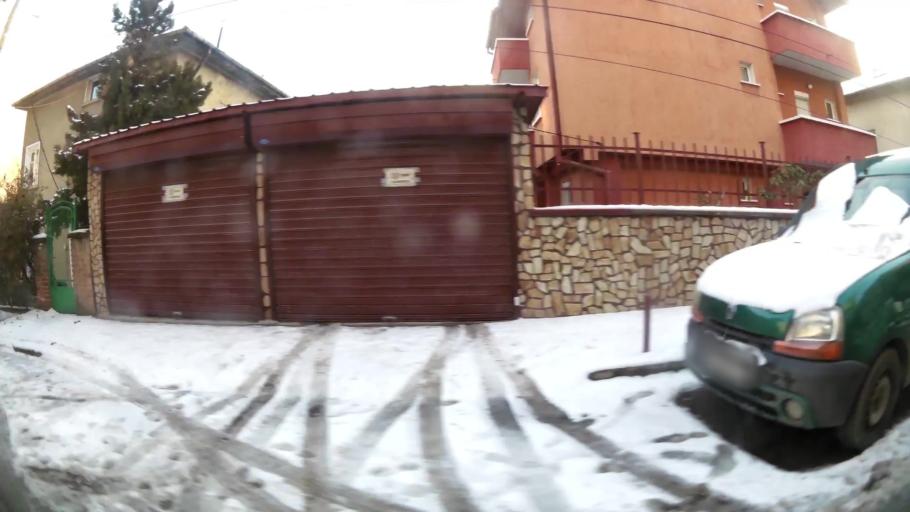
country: BG
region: Sofia-Capital
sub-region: Stolichna Obshtina
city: Sofia
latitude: 42.6859
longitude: 23.3586
